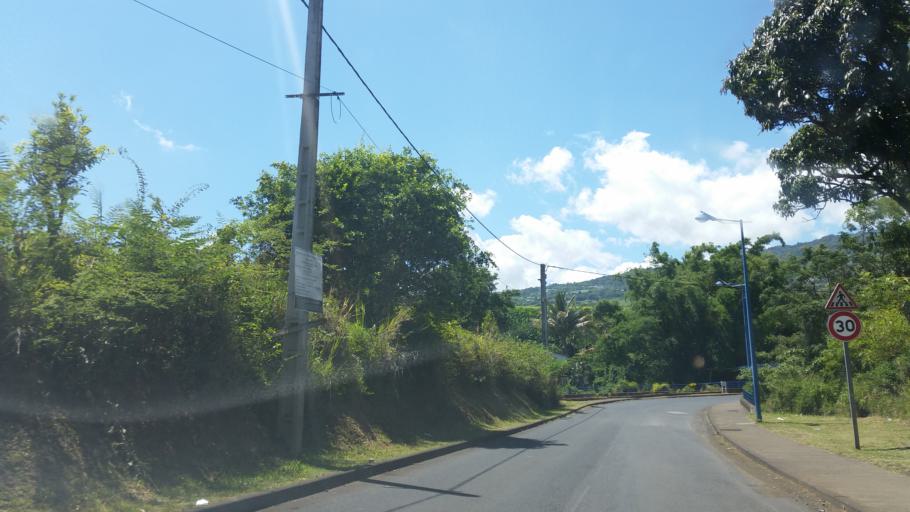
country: RE
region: Reunion
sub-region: Reunion
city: Sainte-Marie
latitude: -20.9260
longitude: 55.5275
